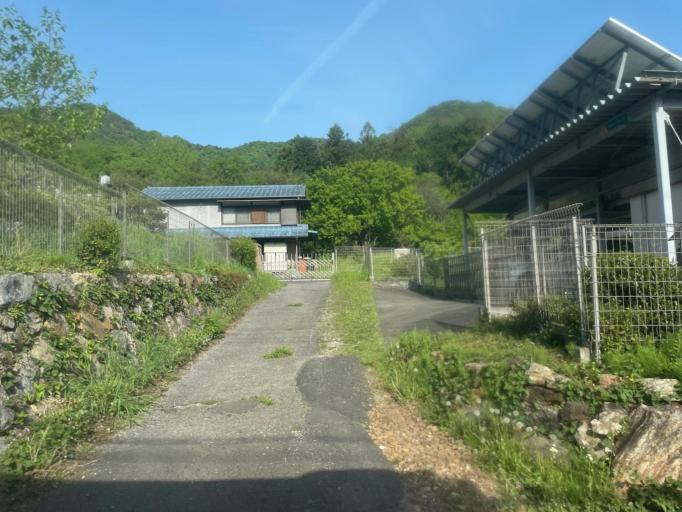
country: JP
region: Tochigi
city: Ashikaga
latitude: 36.3354
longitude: 139.5048
